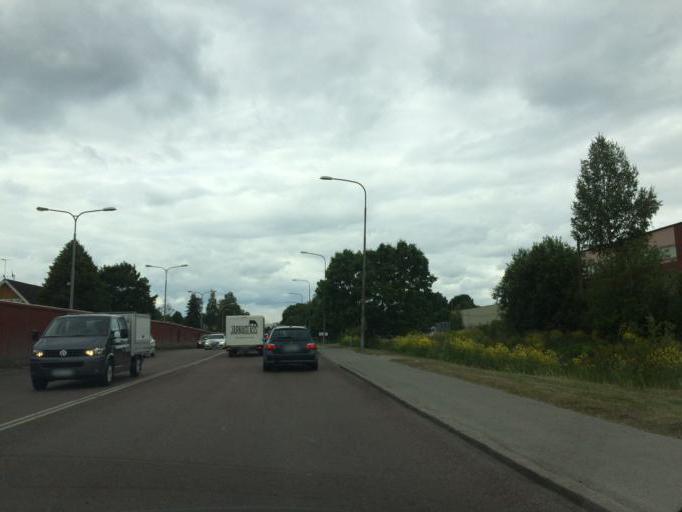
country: SE
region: Stockholm
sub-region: Stockholms Kommun
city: Kista
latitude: 59.3740
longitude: 17.9169
